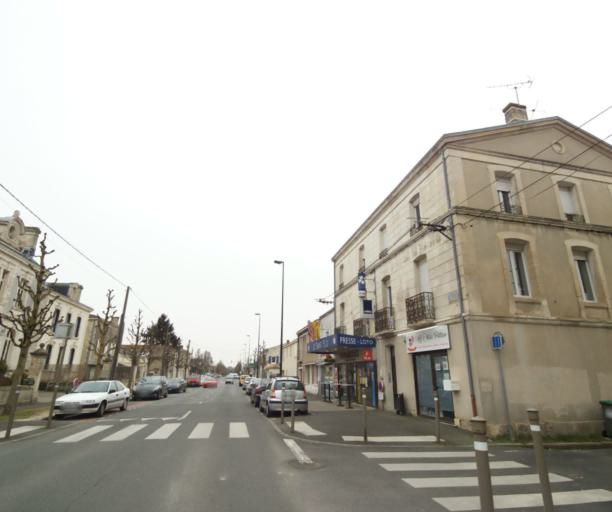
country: FR
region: Poitou-Charentes
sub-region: Departement des Deux-Sevres
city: Niort
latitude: 46.3119
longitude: -0.4657
